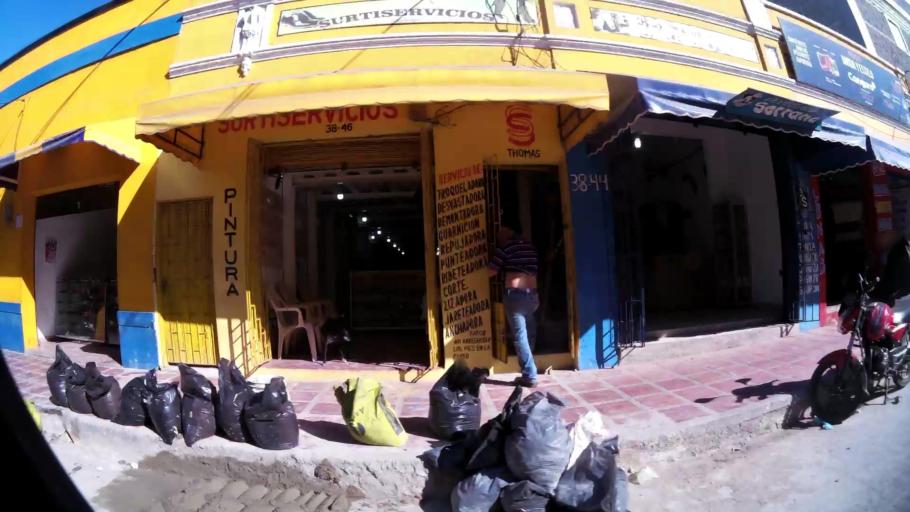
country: CO
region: Atlantico
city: Barranquilla
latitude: 10.9771
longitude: -74.7781
